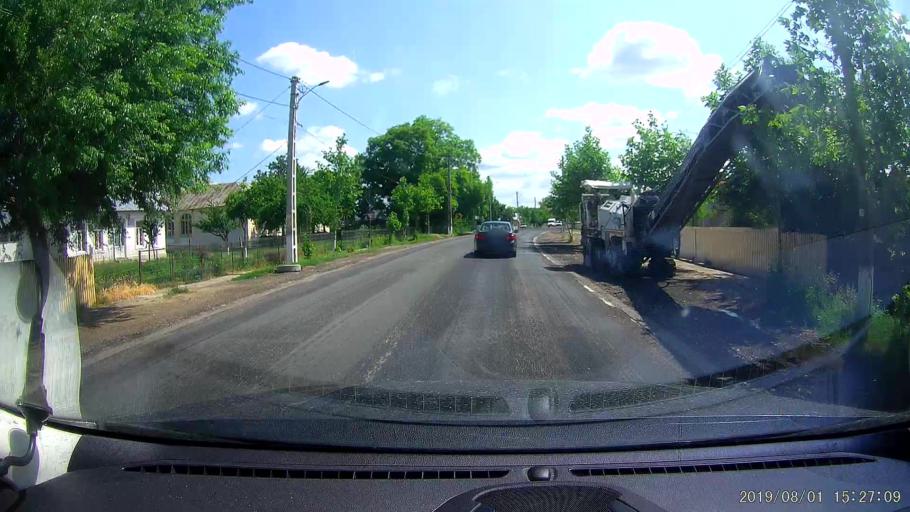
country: RO
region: Braila
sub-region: Comuna Viziru
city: Viziru
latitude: 45.0034
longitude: 27.7168
